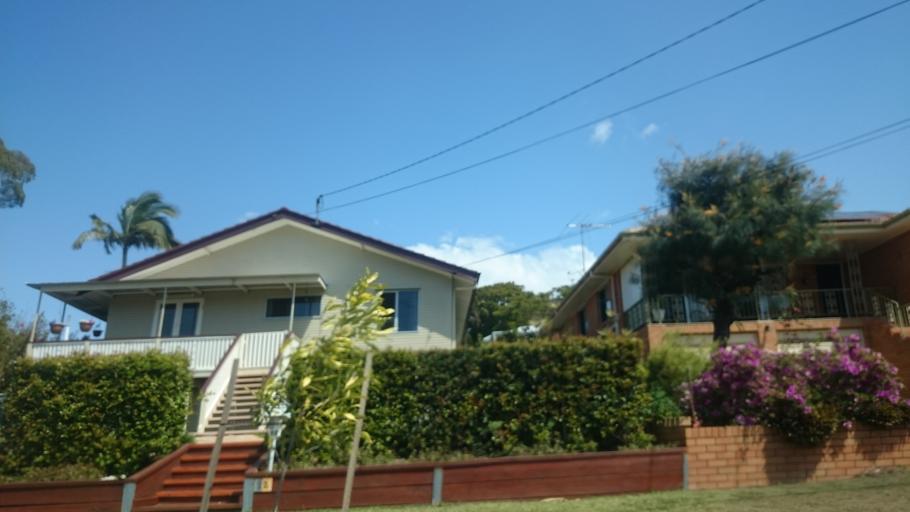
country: AU
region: Queensland
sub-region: Brisbane
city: Manly West
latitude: -27.4660
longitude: 153.1752
